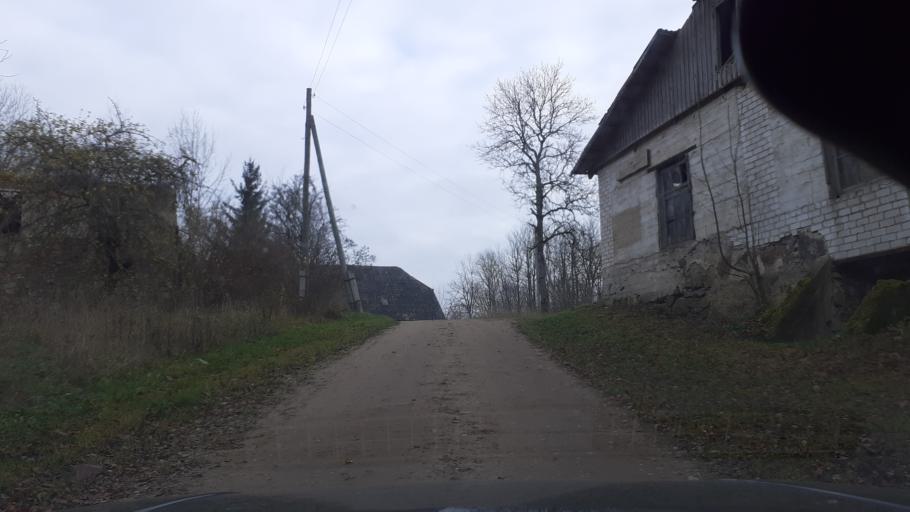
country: LV
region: Aizpute
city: Aizpute
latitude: 56.7837
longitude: 21.7553
